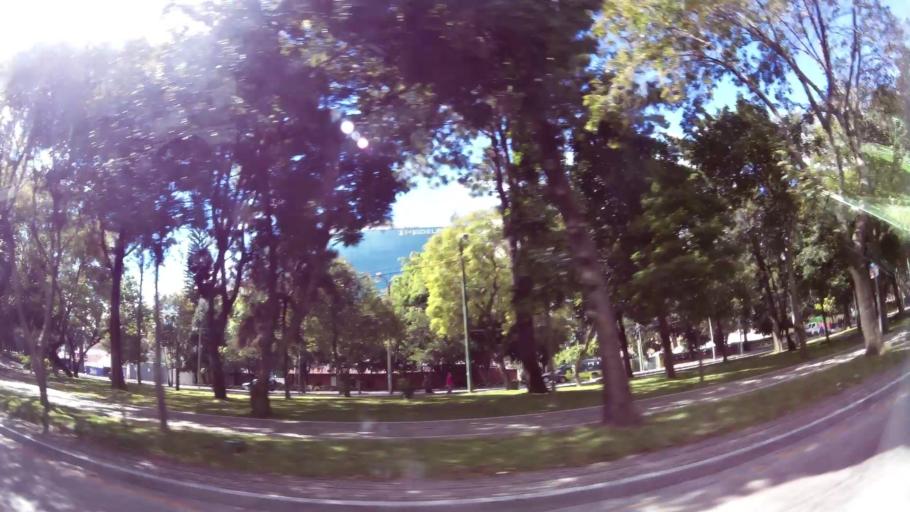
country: GT
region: Guatemala
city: Guatemala City
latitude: 14.6020
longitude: -90.5162
